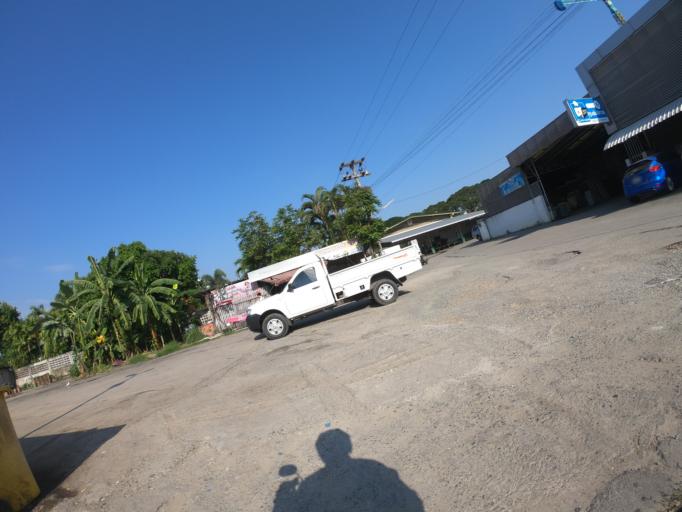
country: TH
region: Chiang Mai
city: Chiang Mai
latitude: 18.8036
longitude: 99.0169
